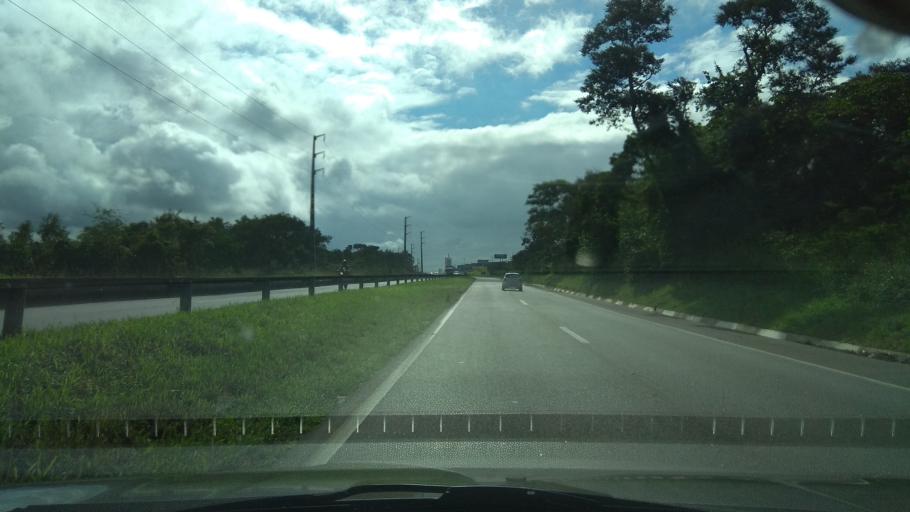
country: BR
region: Bahia
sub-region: Conceicao Do Jacuipe
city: Conceicao do Jacuipe
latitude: -12.3473
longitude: -38.8374
